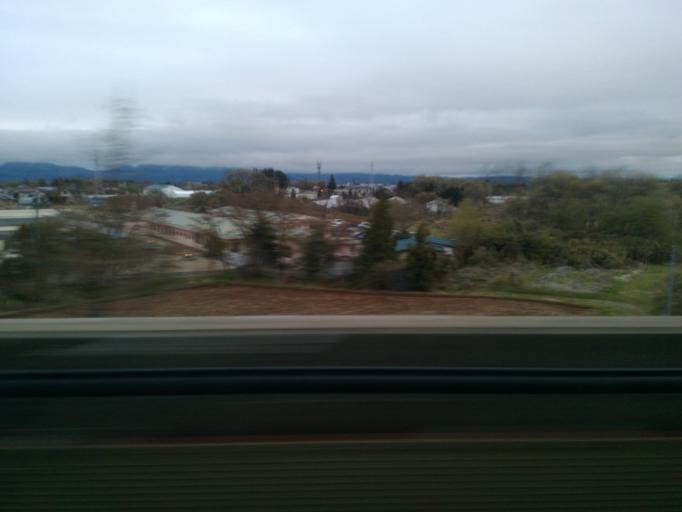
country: JP
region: Fukushima
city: Sukagawa
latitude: 37.3032
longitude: 140.3420
